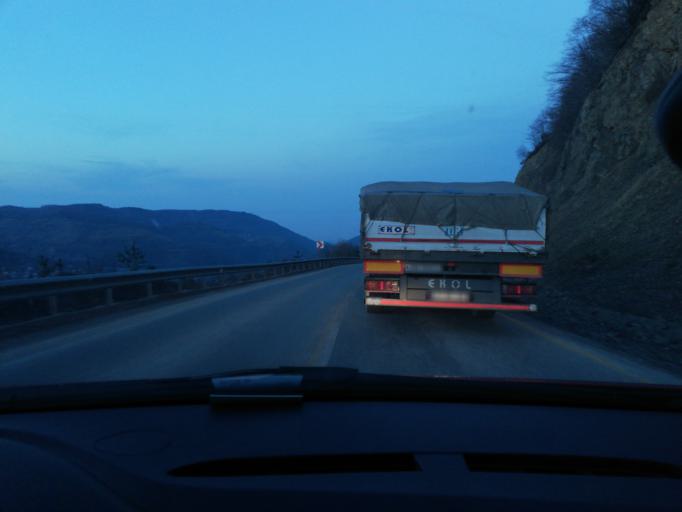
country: TR
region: Kastamonu
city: Inebolu
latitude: 41.9162
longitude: 33.7269
